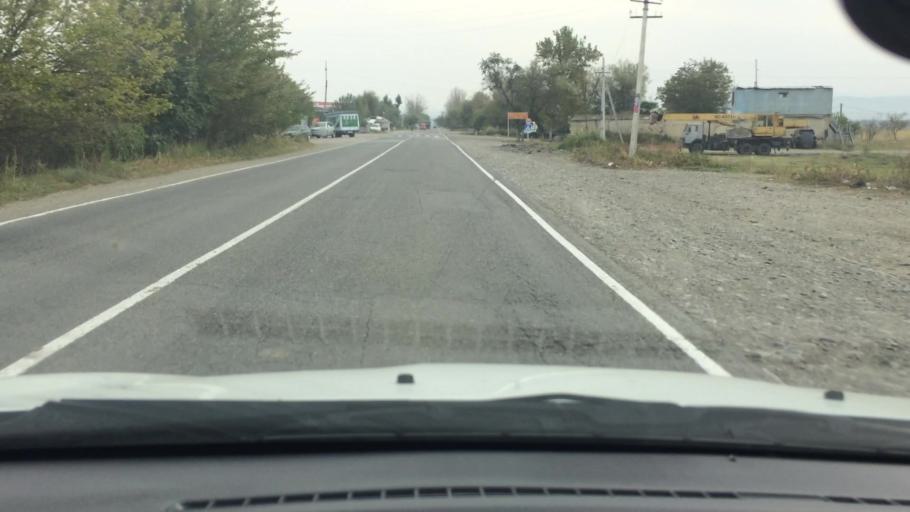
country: GE
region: Kvemo Kartli
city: Rust'avi
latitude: 41.4512
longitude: 44.9931
